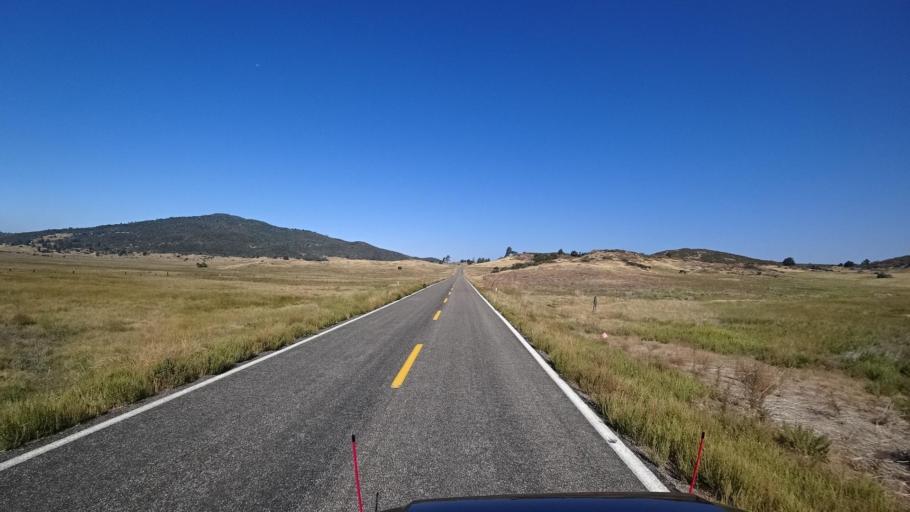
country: US
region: California
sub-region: San Diego County
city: Julian
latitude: 33.0011
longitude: -116.5517
